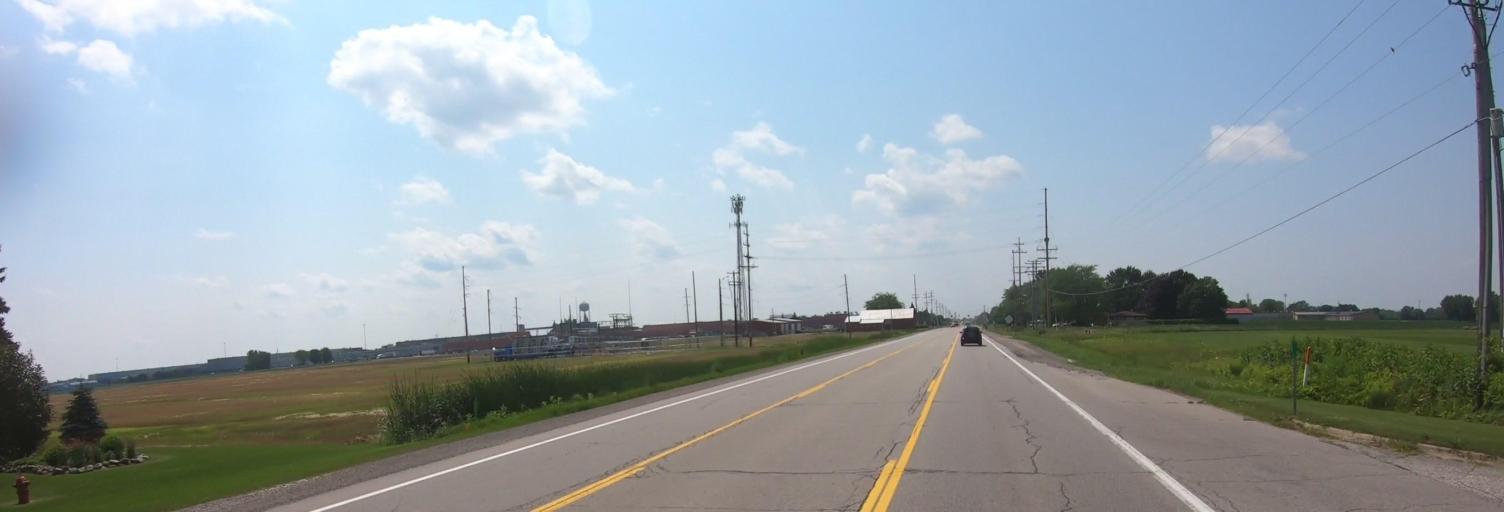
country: US
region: Michigan
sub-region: Saginaw County
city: Buena Vista
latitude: 43.4146
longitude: -83.8715
